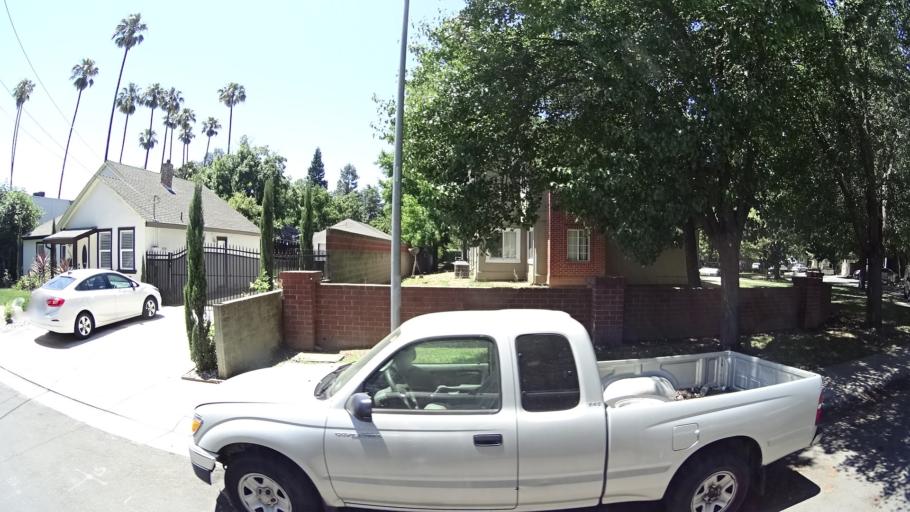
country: US
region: California
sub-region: Yolo County
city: West Sacramento
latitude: 38.5333
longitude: -121.5198
